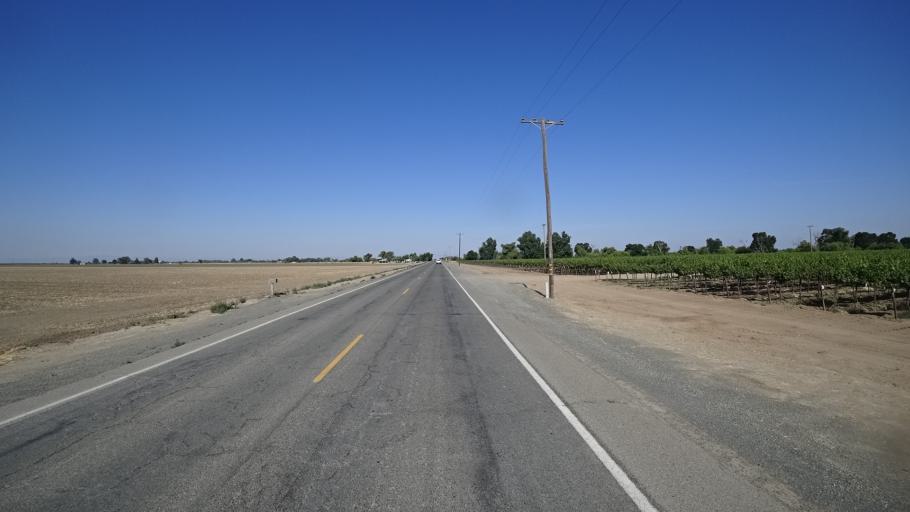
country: US
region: California
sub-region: Kings County
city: Lemoore
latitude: 36.3440
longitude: -119.8565
